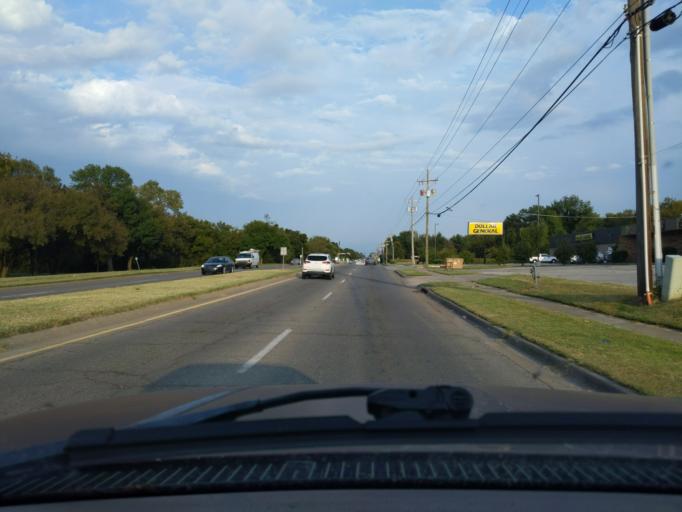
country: US
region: Oklahoma
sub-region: Tulsa County
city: Broken Arrow
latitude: 36.1334
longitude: -95.8453
